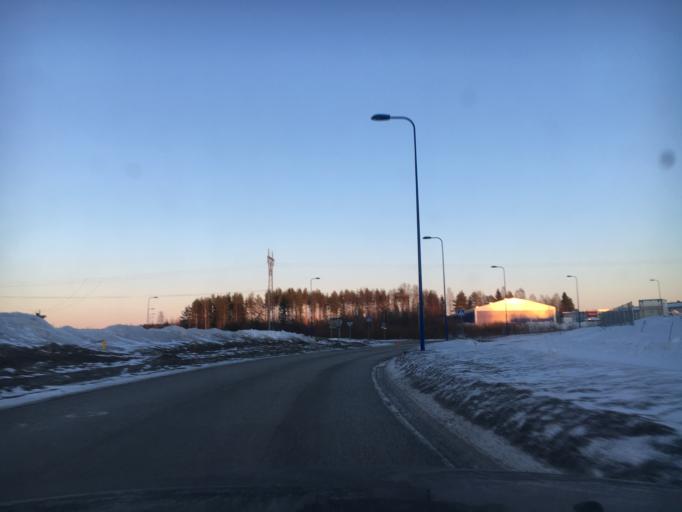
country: FI
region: Kainuu
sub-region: Kajaani
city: Kajaani
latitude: 64.2231
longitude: 27.7801
